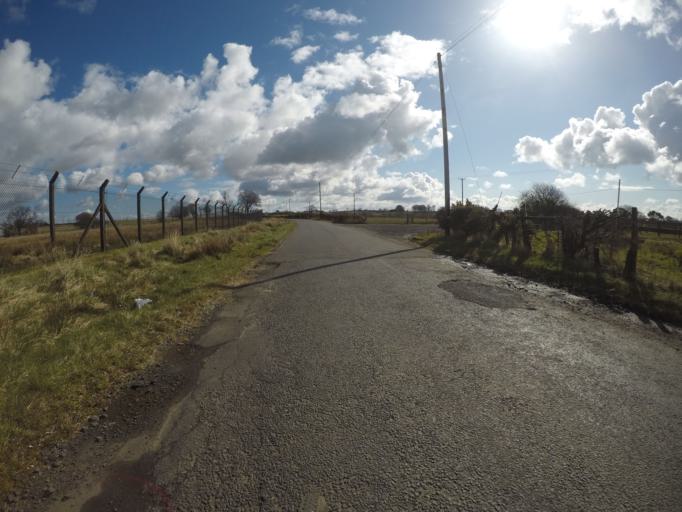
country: GB
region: Scotland
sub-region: North Ayrshire
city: Beith
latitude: 55.7222
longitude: -4.6140
